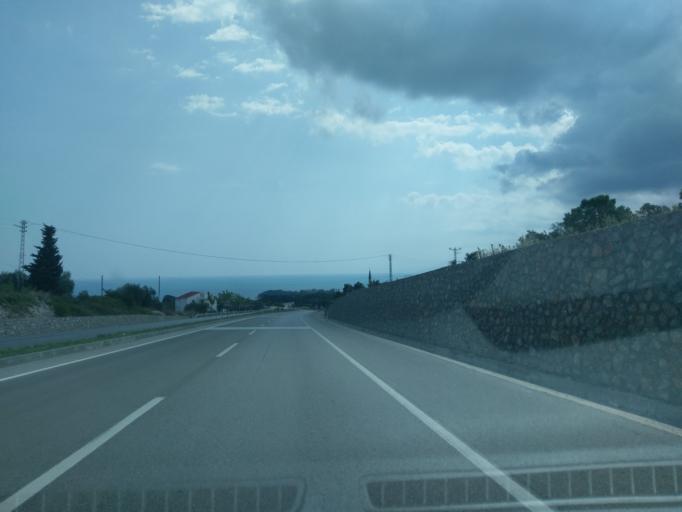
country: TR
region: Sinop
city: Kabali
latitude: 41.8487
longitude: 35.1274
